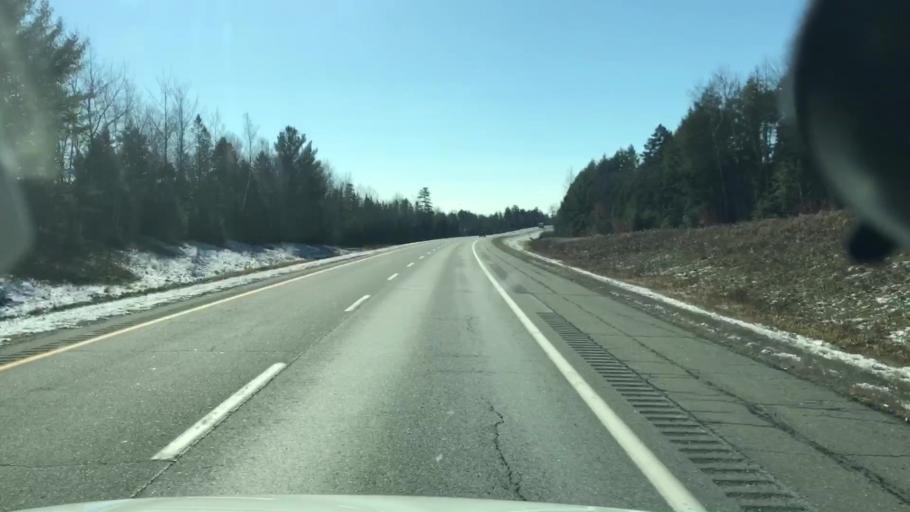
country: US
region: Maine
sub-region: Penobscot County
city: Howland
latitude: 45.2895
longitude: -68.6663
